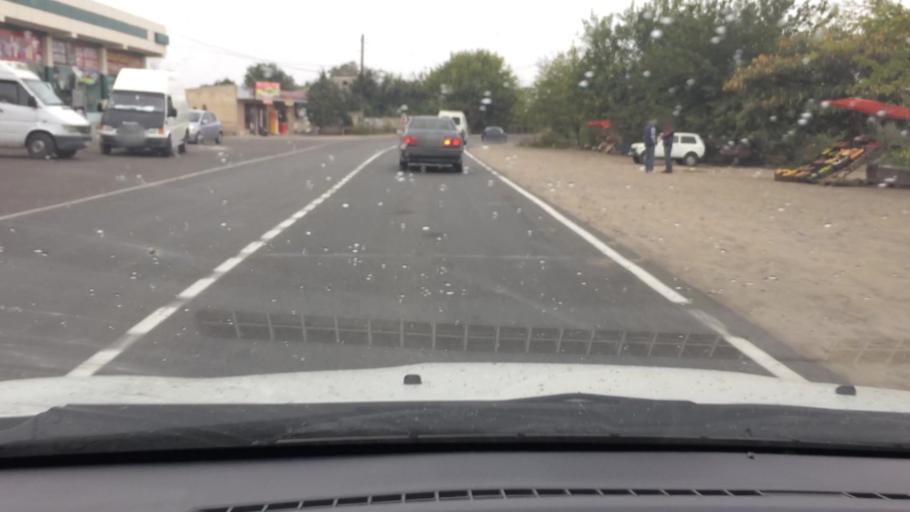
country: GE
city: Naghvarevi
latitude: 41.3990
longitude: 44.8247
